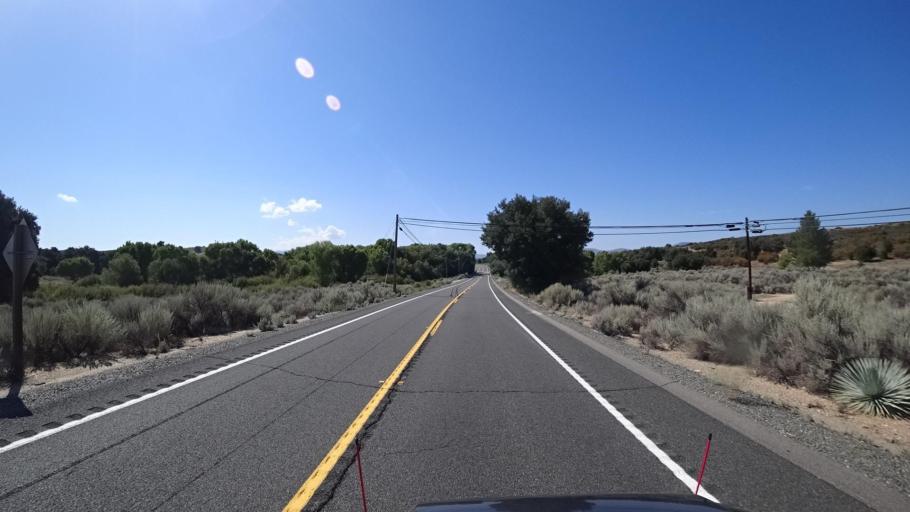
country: US
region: California
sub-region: Riverside County
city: Aguanga
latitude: 33.3119
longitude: -116.6926
